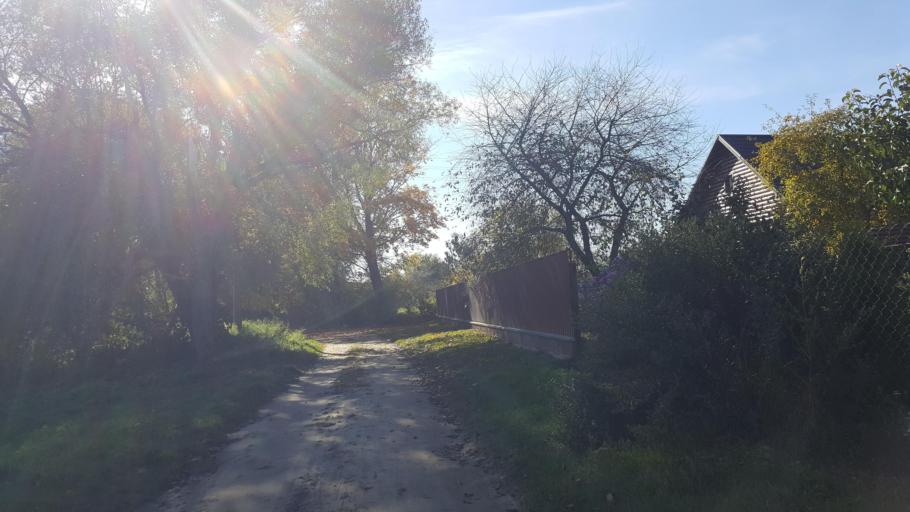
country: BY
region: Brest
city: Kamyanyets
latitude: 52.4042
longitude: 23.8016
